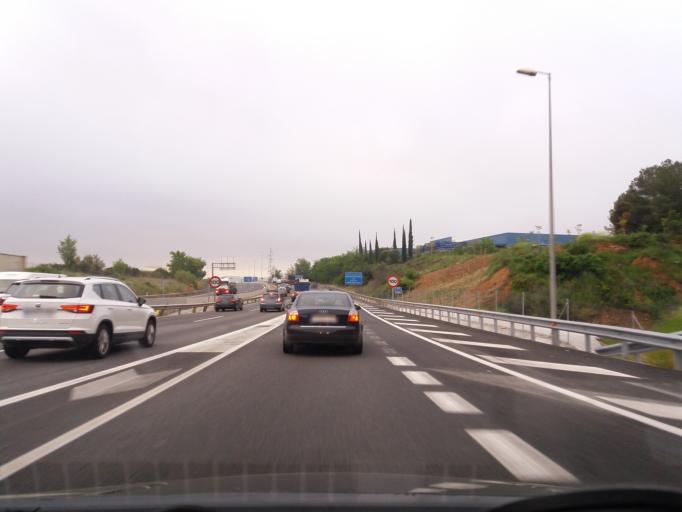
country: ES
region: Catalonia
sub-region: Provincia de Barcelona
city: Abrera
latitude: 41.5134
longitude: 1.8993
